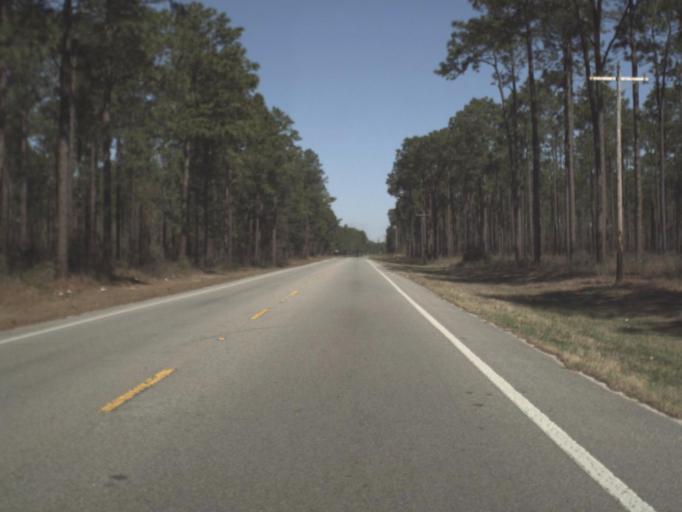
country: US
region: Florida
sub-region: Leon County
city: Woodville
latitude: 30.3338
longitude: -84.3113
